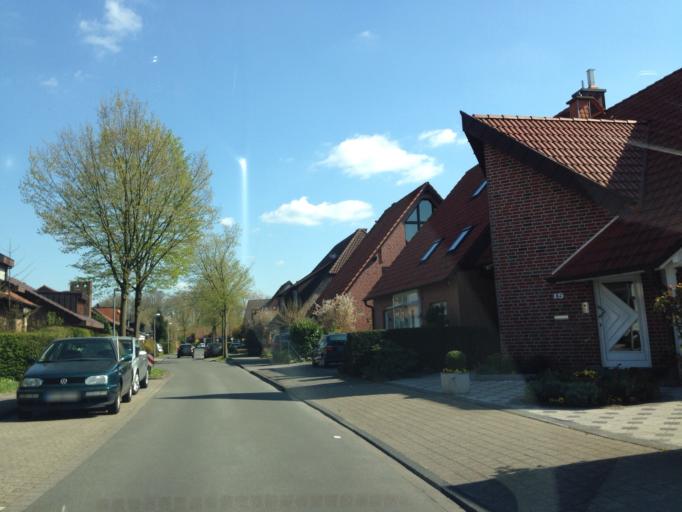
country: DE
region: North Rhine-Westphalia
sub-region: Regierungsbezirk Munster
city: Muenster
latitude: 51.9931
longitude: 7.5953
